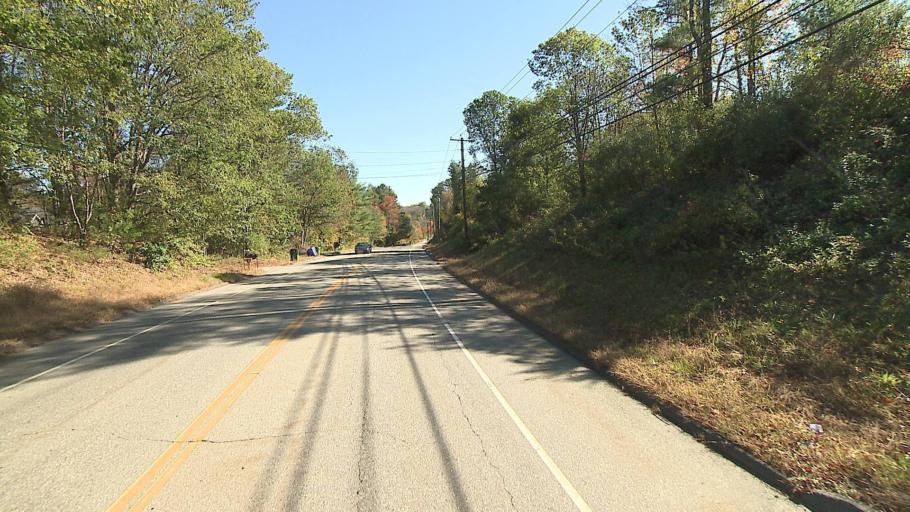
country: US
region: Connecticut
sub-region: Tolland County
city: Hebron
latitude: 41.6574
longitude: -72.3781
